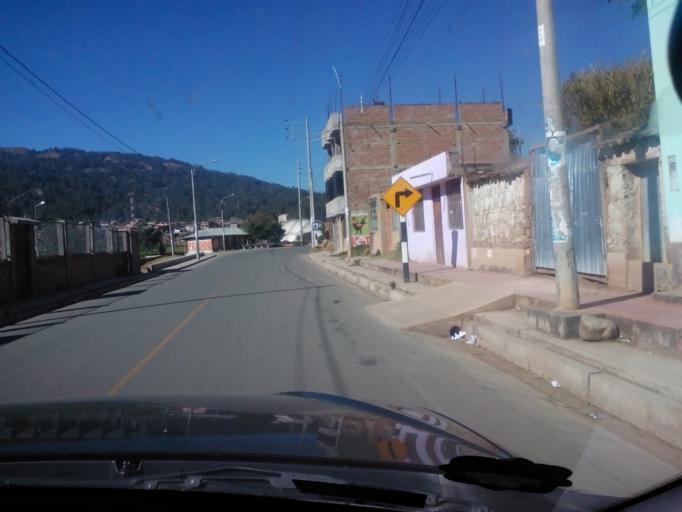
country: PE
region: Apurimac
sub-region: Provincia de Andahuaylas
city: Talavera
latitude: -13.6587
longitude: -73.4344
